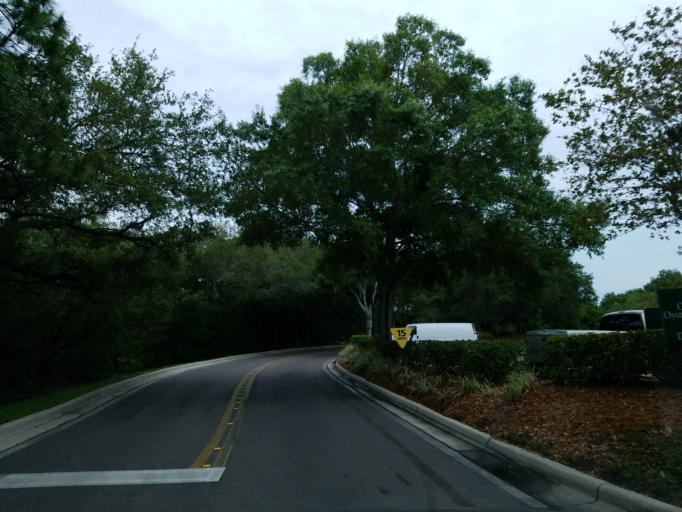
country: US
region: Florida
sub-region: Hillsborough County
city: Town 'n' Country
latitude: 27.9646
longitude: -82.5488
